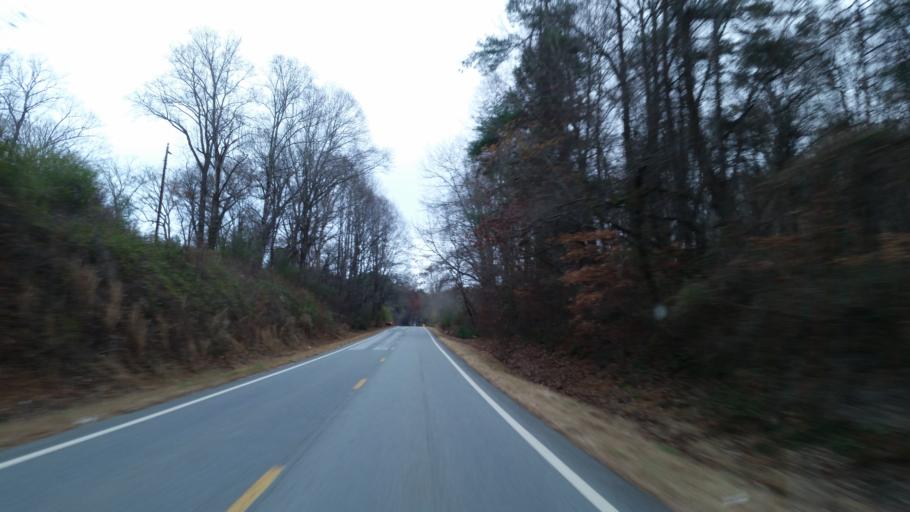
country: US
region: Georgia
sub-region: Dawson County
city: Dawsonville
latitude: 34.4957
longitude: -84.1948
